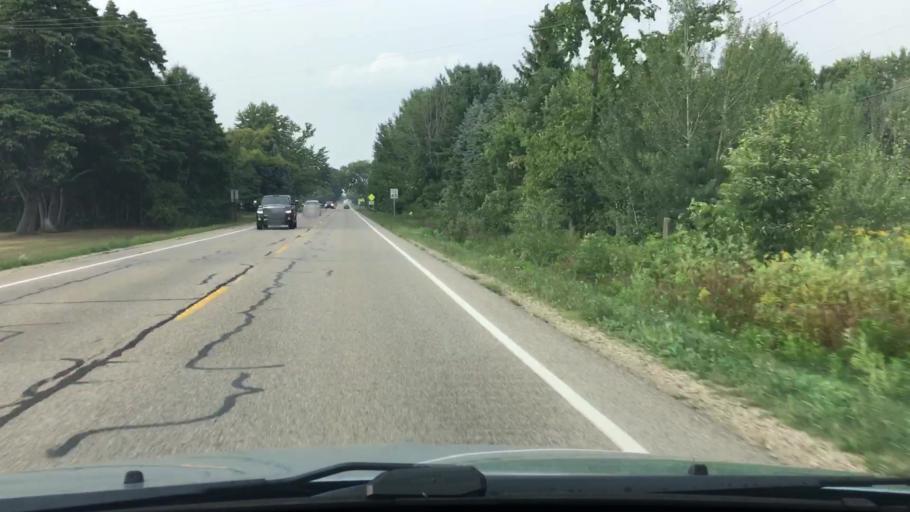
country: US
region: Michigan
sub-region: Ottawa County
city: Hudsonville
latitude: 42.9120
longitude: -85.9023
